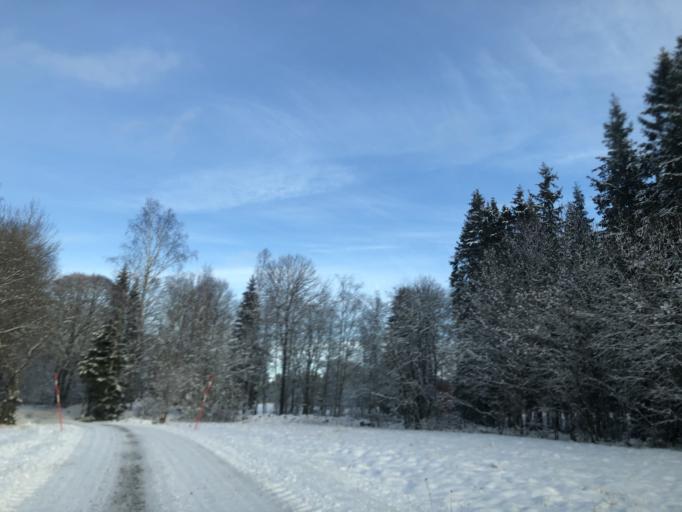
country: SE
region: Vaestra Goetaland
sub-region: Ulricehamns Kommun
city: Ulricehamn
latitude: 57.7449
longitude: 13.5067
